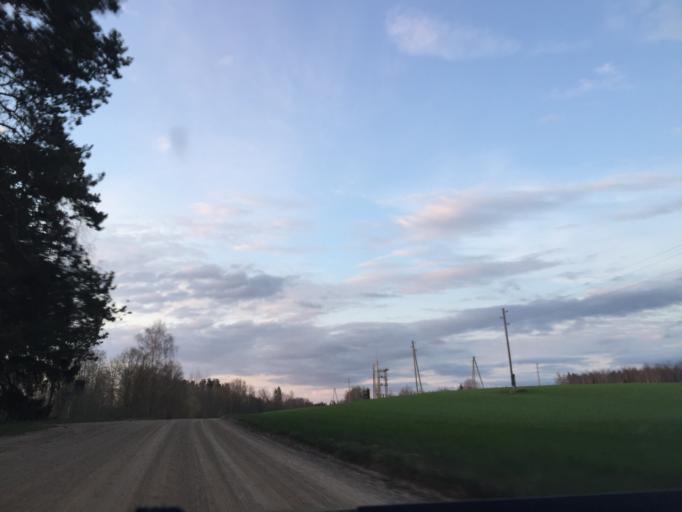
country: LV
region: Aluksnes Rajons
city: Aluksne
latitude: 57.3248
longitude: 26.9421
